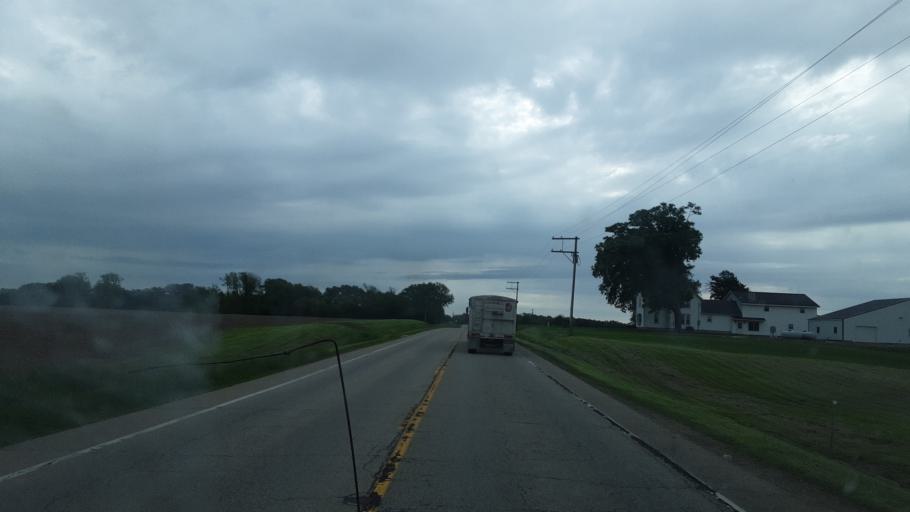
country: US
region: Illinois
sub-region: Fulton County
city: Lewistown
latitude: 40.3045
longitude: -90.1855
